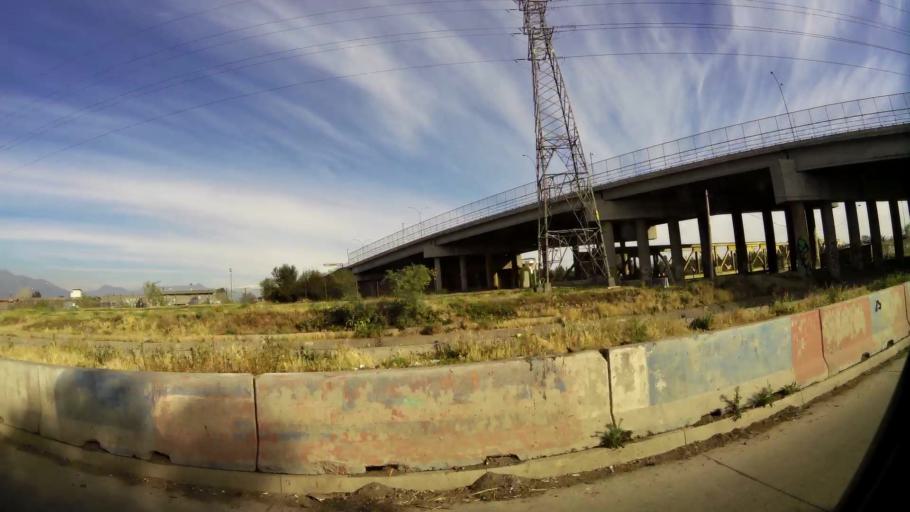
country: CL
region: Santiago Metropolitan
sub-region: Provincia de Santiago
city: Lo Prado
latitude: -33.4795
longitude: -70.7004
